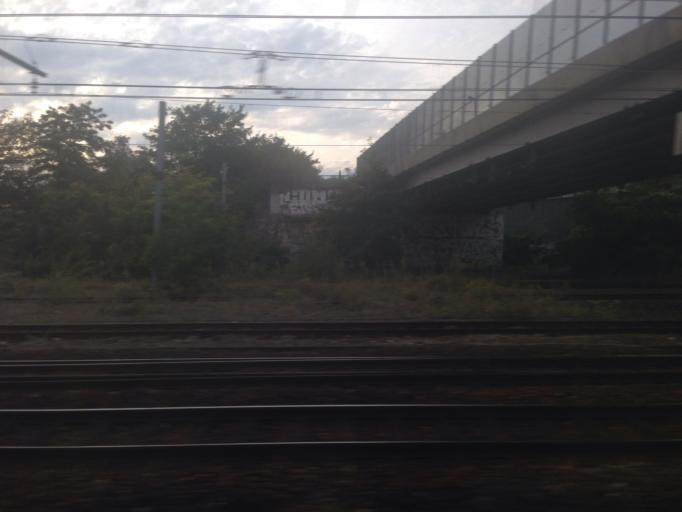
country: FR
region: Ile-de-France
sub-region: Departement de l'Essonne
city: Athis-Mons
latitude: 48.7055
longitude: 2.3974
